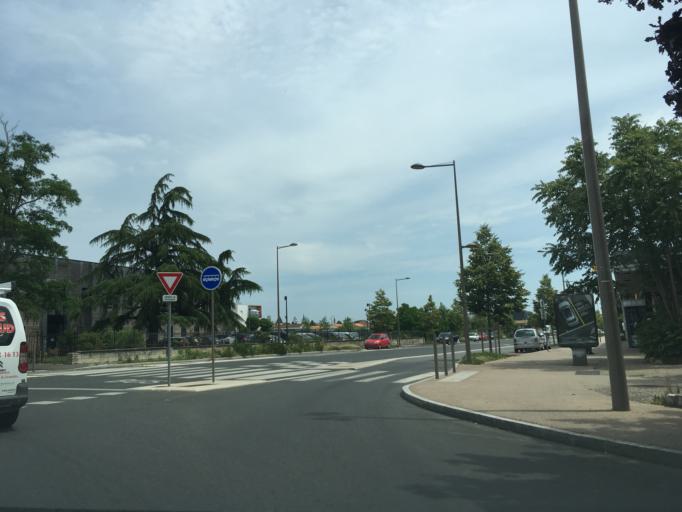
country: FR
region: Poitou-Charentes
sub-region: Departement des Deux-Sevres
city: Niort
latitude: 46.3167
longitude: -0.4805
